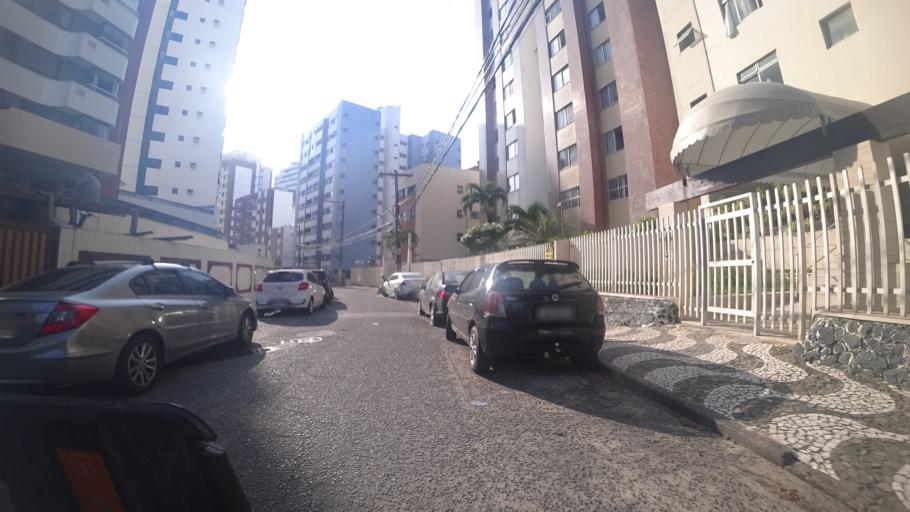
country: BR
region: Bahia
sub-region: Salvador
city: Salvador
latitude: -12.9973
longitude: -38.4521
